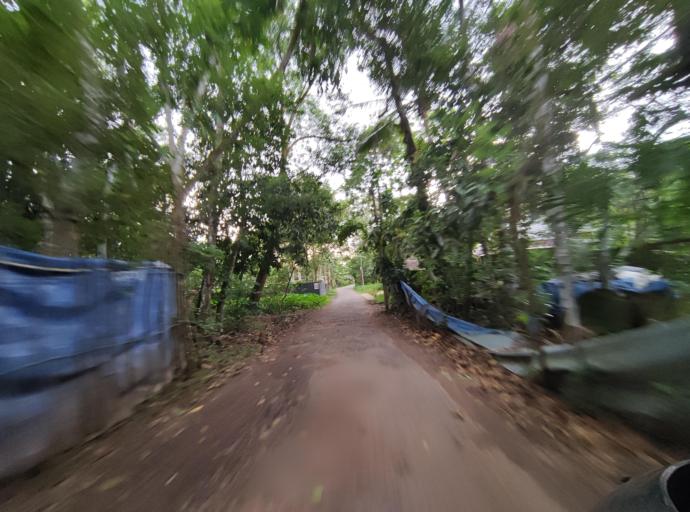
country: IN
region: Kerala
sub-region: Alappuzha
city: Shertallai
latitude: 9.6678
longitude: 76.3373
